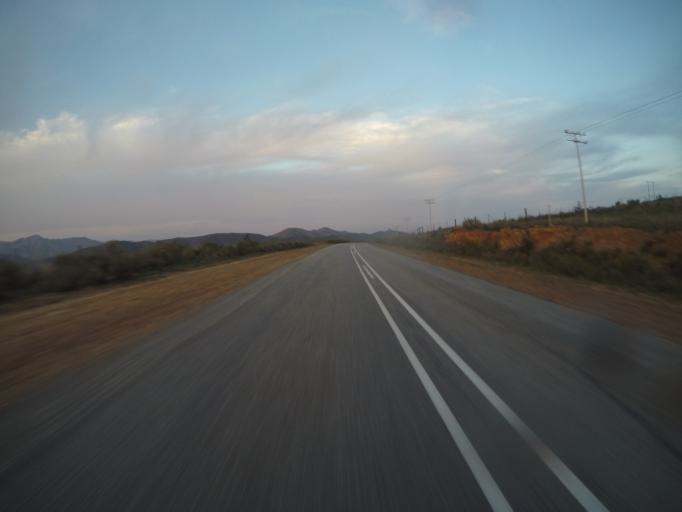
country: ZA
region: Western Cape
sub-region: Eden District Municipality
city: Plettenberg Bay
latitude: -33.7428
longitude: 23.4606
